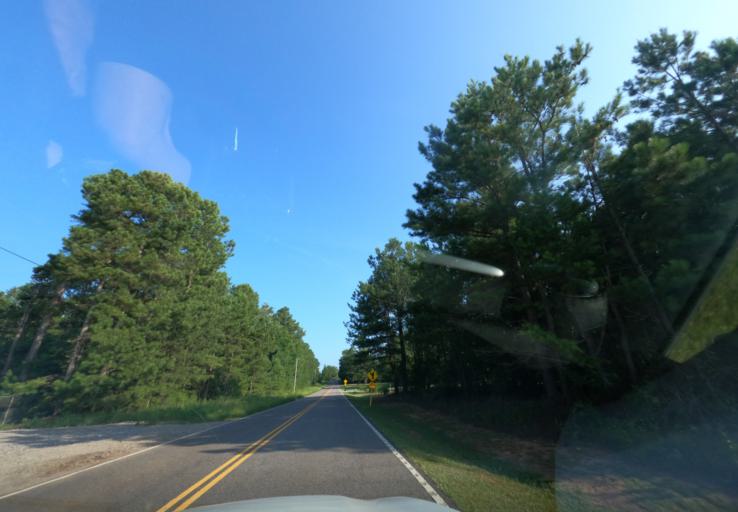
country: US
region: South Carolina
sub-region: Edgefield County
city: Murphys Estates
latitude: 33.6357
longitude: -81.9754
